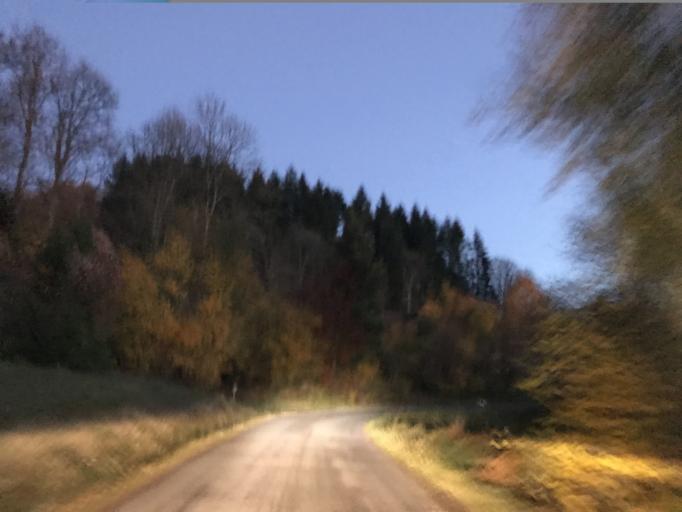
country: FR
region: Rhone-Alpes
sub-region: Departement de la Loire
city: Noiretable
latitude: 45.7546
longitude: 3.6998
